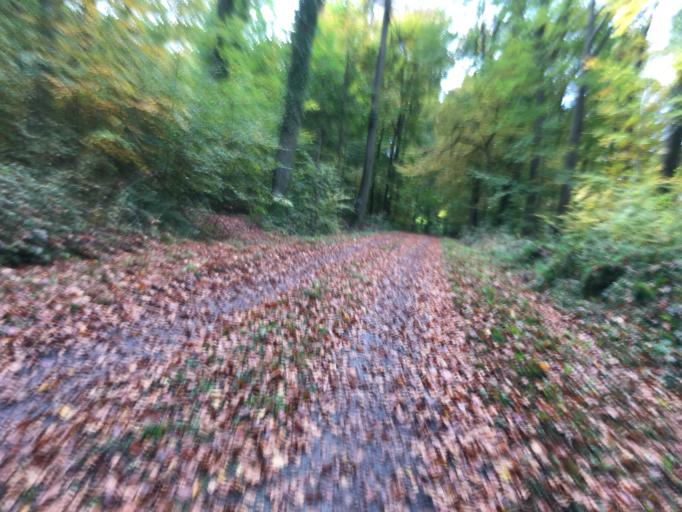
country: DE
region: Baden-Wuerttemberg
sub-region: Karlsruhe Region
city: Waibstadt
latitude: 49.2723
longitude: 8.9238
